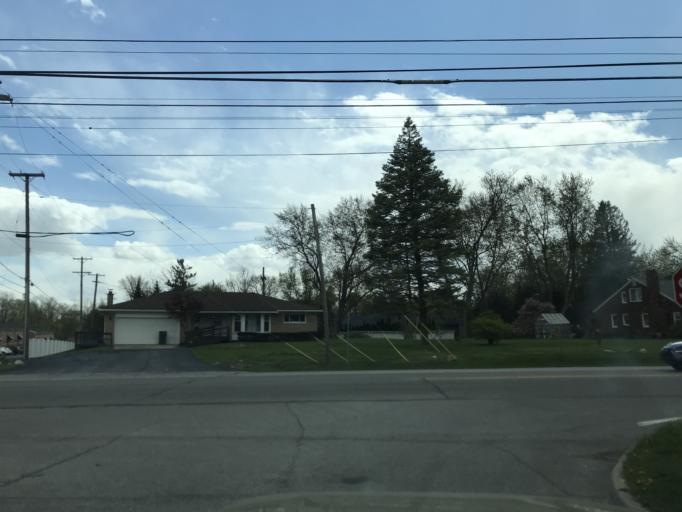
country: US
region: Michigan
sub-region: Wayne County
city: Plymouth
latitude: 42.3759
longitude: -83.4842
